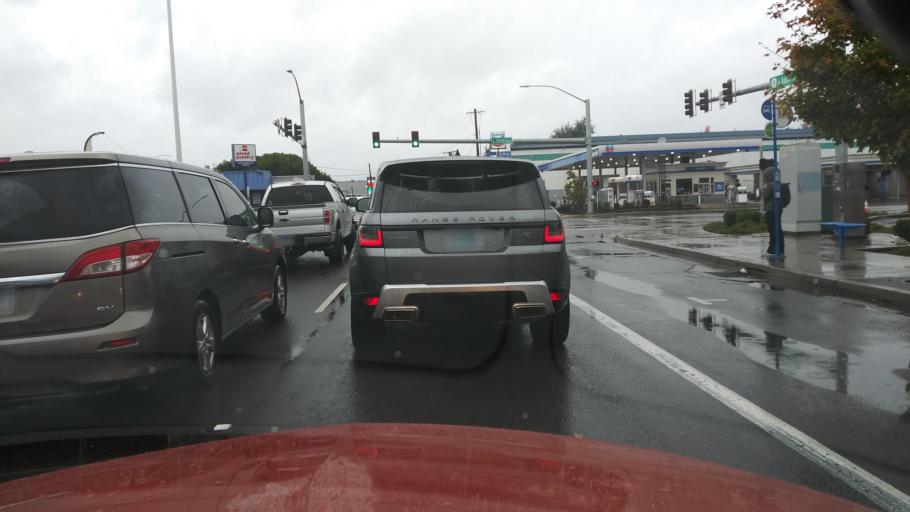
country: US
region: Oregon
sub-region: Washington County
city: Cornelius
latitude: 45.5210
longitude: -123.0588
